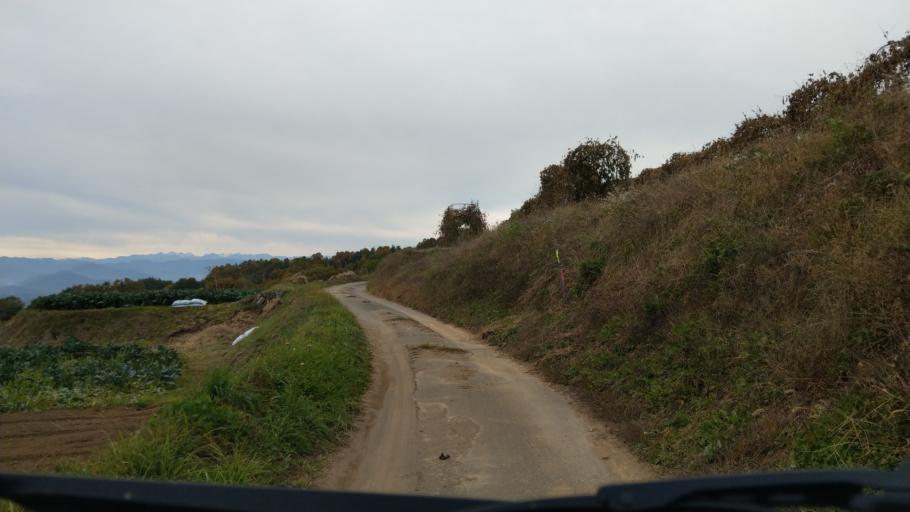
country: JP
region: Nagano
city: Komoro
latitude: 36.3600
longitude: 138.4299
